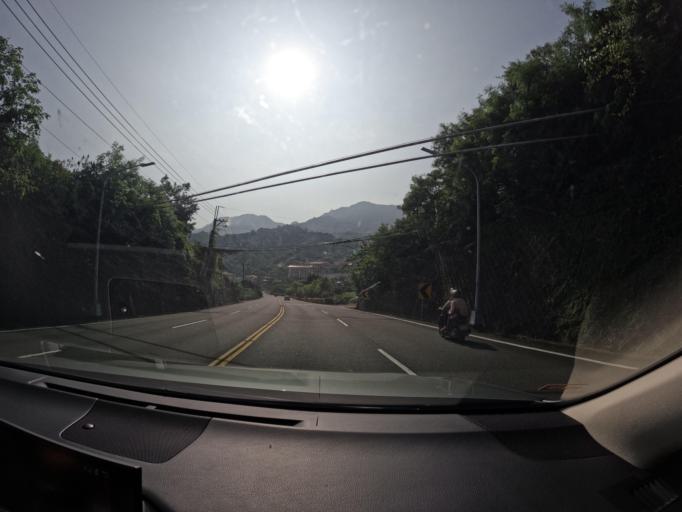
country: TW
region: Taiwan
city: Yujing
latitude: 23.0710
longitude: 120.5102
